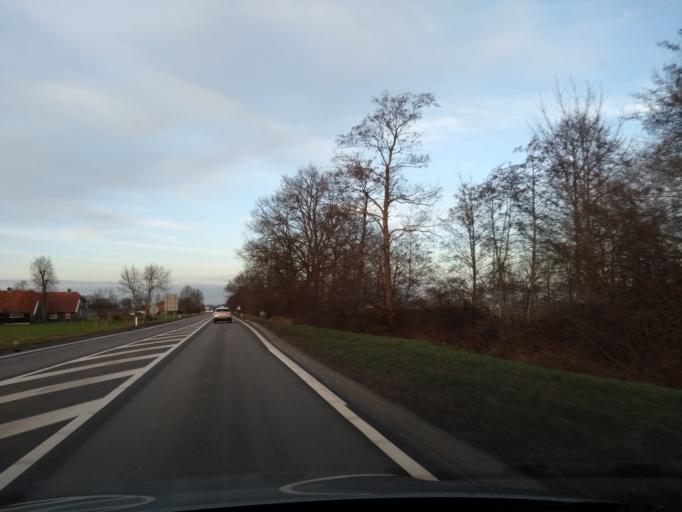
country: NL
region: Overijssel
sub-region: Gemeente Twenterand
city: Den Ham
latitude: 52.5807
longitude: 6.4144
